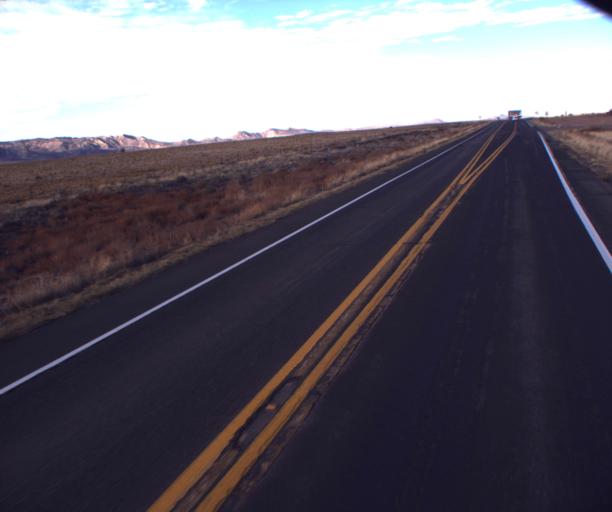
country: US
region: Arizona
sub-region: Apache County
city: Lukachukai
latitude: 36.9608
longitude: -109.3797
